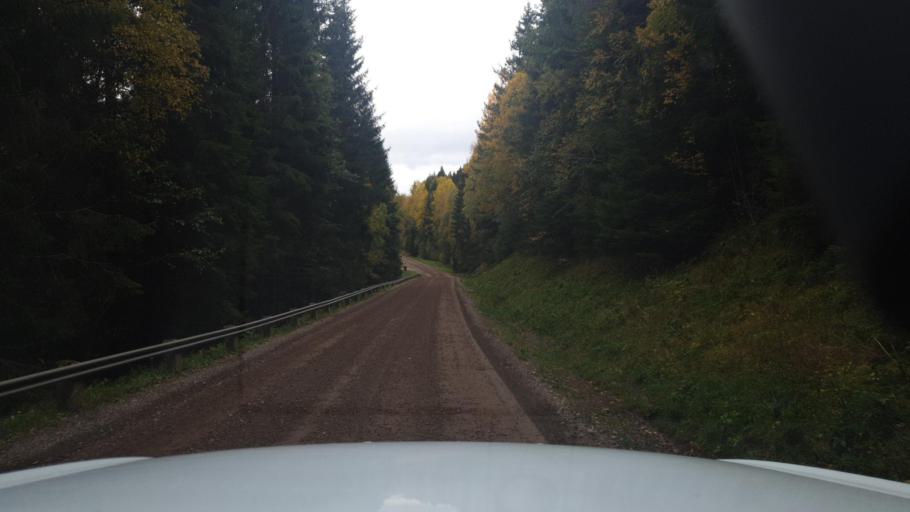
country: SE
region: Vaermland
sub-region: Eda Kommun
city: Charlottenberg
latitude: 60.0618
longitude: 12.5488
